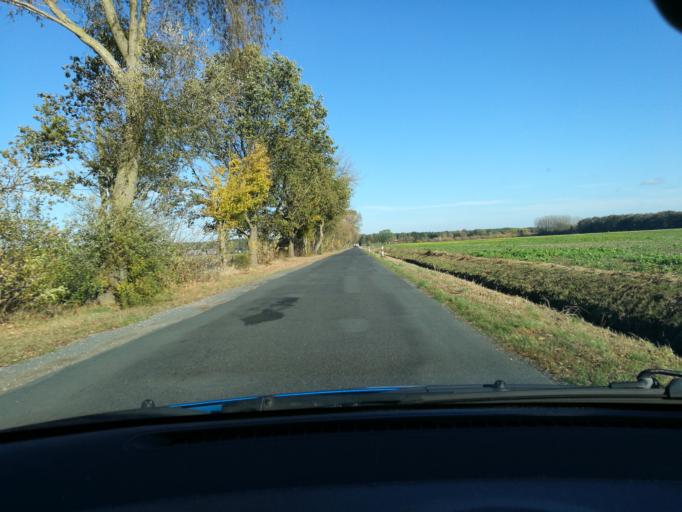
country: DE
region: Mecklenburg-Vorpommern
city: Neu Kaliss
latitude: 53.1519
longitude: 11.3093
